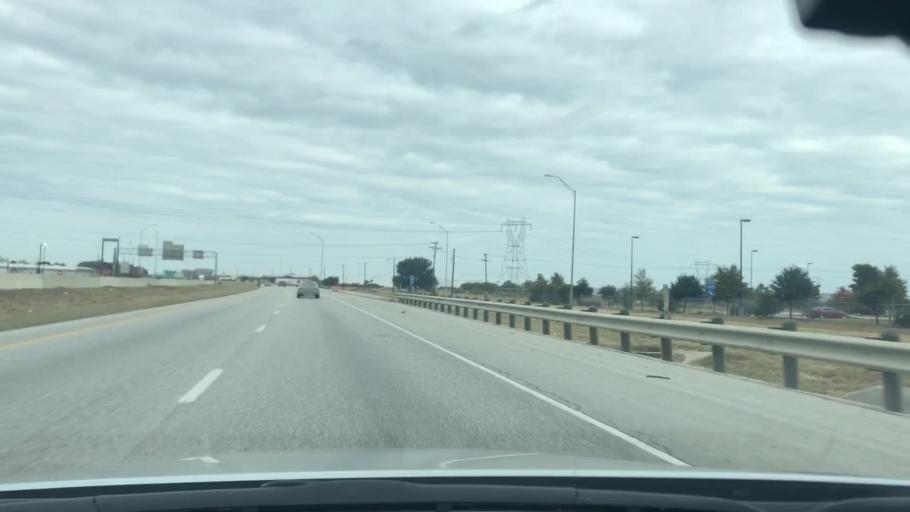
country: US
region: Texas
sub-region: Bexar County
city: Kirby
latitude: 29.4407
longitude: -98.3945
